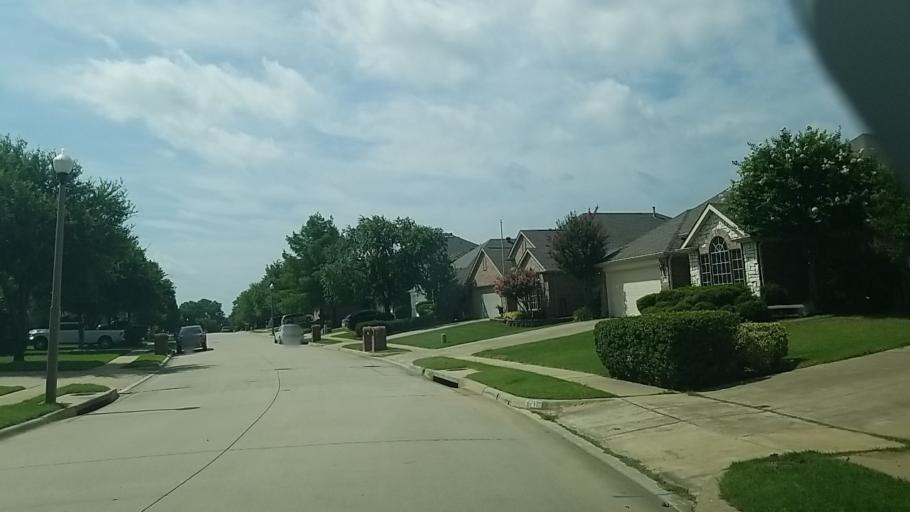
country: US
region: Texas
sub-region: Denton County
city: Corinth
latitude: 33.1489
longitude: -97.0958
